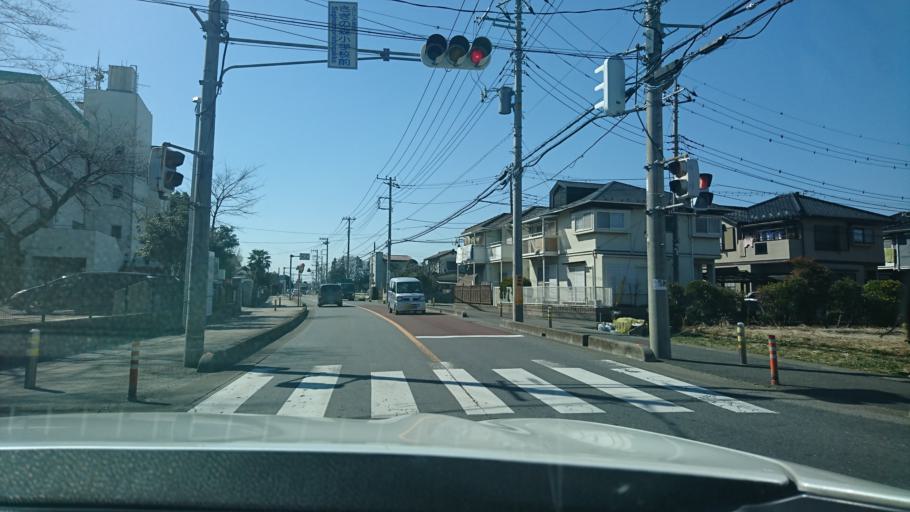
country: JP
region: Saitama
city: Kamifukuoka
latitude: 35.8703
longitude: 139.5401
